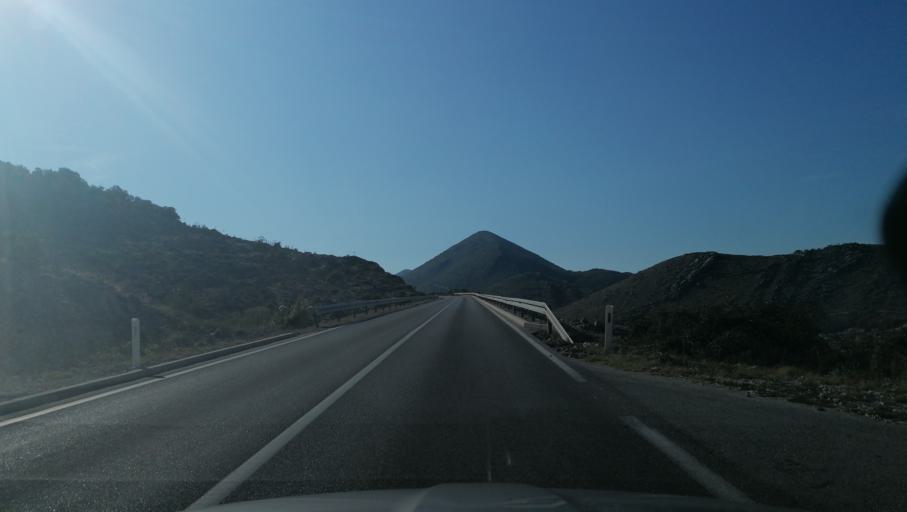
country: BA
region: Republika Srpska
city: Trebinje
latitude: 42.6728
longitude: 18.3469
